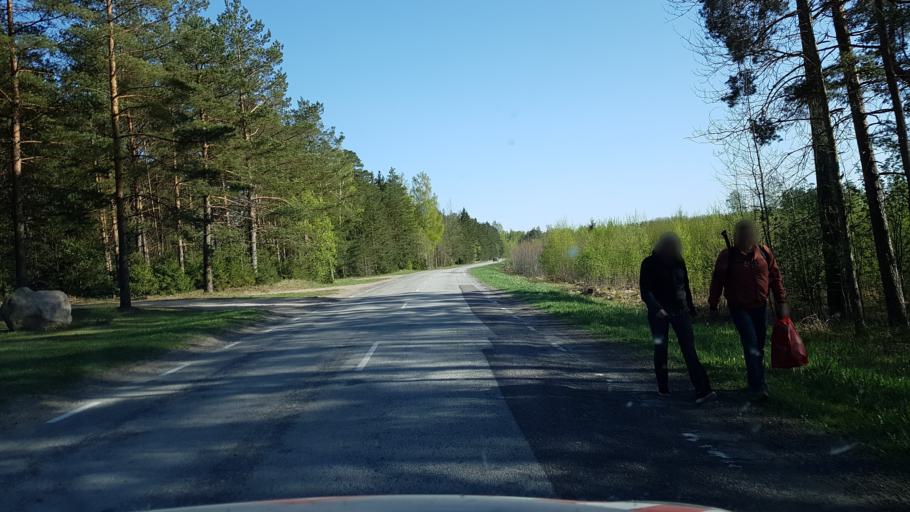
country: EE
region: Paernumaa
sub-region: Paikuse vald
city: Paikuse
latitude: 58.3539
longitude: 24.6648
